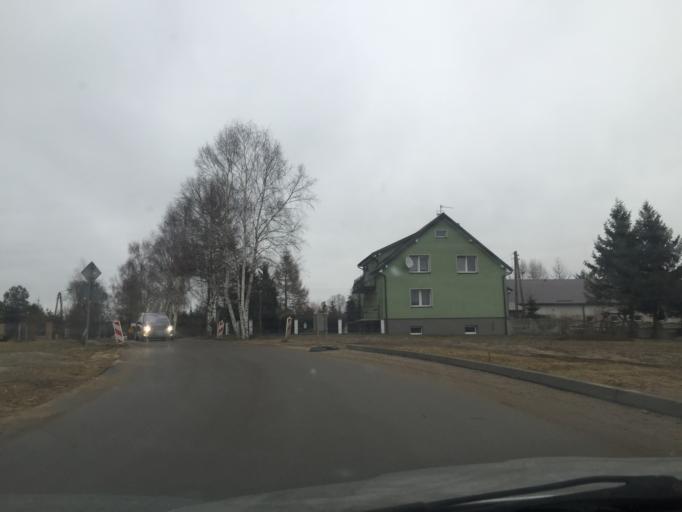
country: PL
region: Pomeranian Voivodeship
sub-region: Powiat kartuski
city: Banino
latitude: 54.3929
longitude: 18.4307
